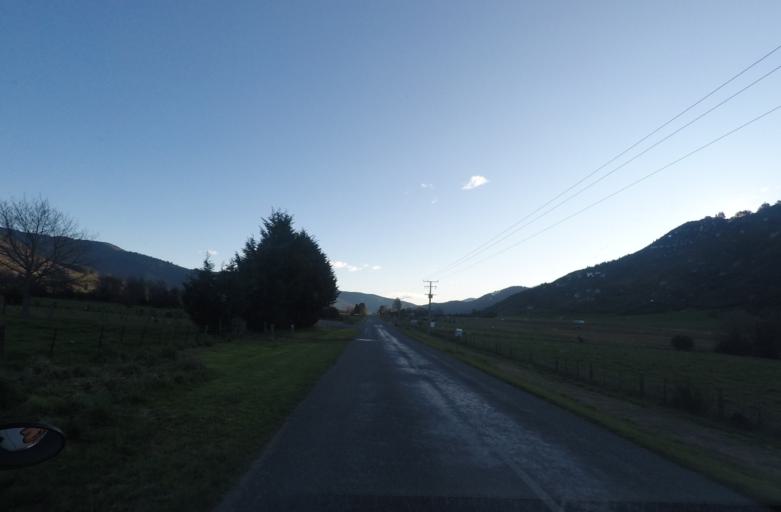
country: NZ
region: Marlborough
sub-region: Marlborough District
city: Picton
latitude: -41.2901
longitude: 173.8870
